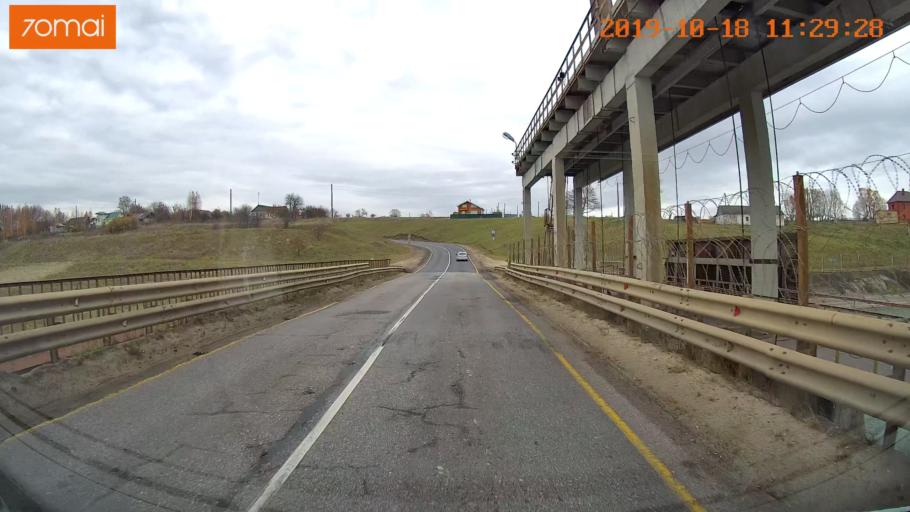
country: RU
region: Rjazan
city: Oktyabr'skiy
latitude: 54.1562
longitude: 38.6774
